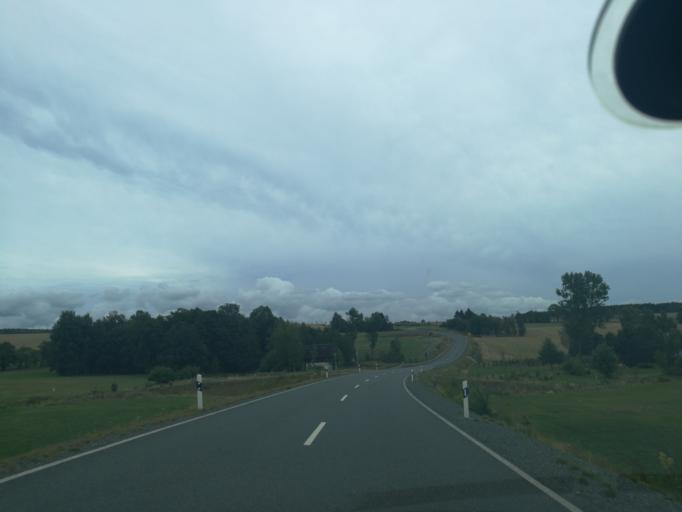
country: DE
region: Bavaria
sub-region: Upper Franconia
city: Regnitzlosau
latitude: 50.3383
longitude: 12.0765
